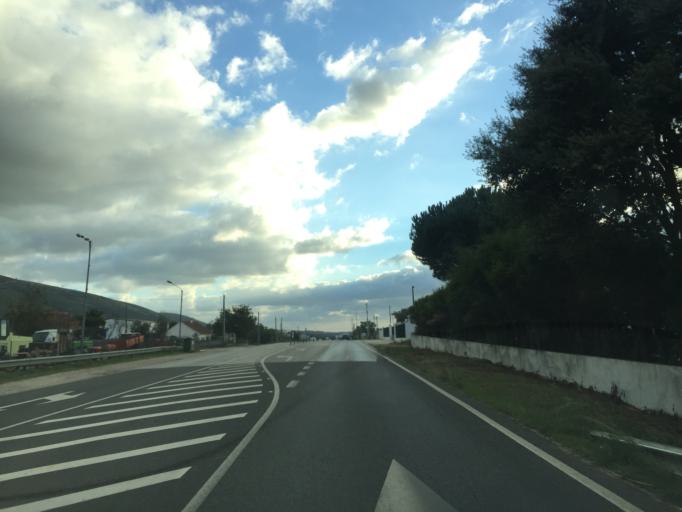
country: PT
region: Leiria
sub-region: Alcobaca
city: Aljubarrota
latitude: 39.5647
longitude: -8.8824
